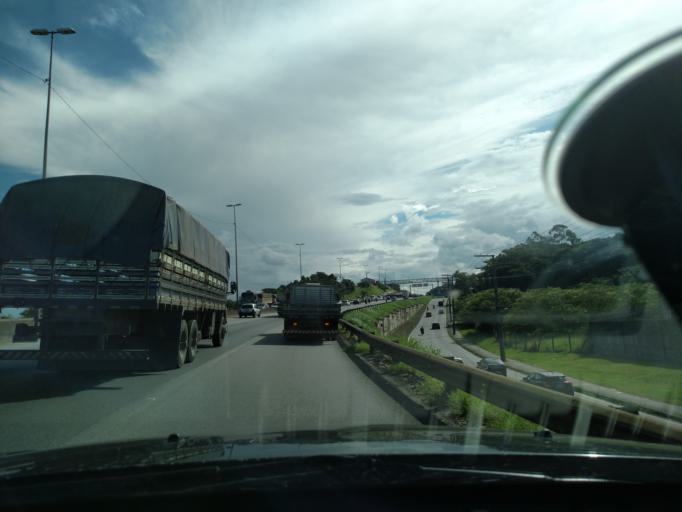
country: BR
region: Santa Catarina
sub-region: Sao Jose
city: Campinas
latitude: -27.6008
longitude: -48.6237
